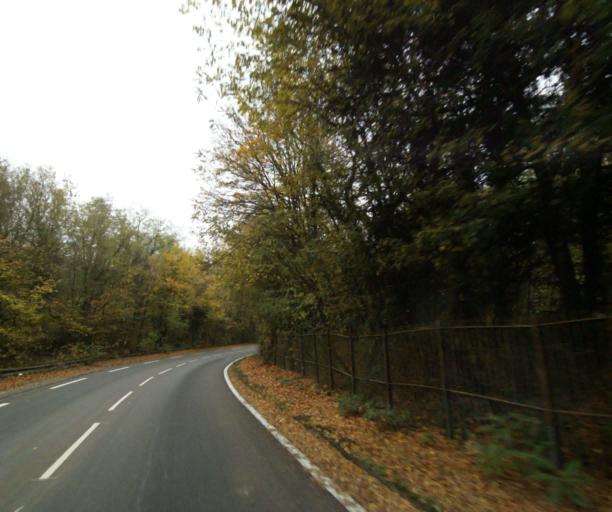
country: FR
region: Lorraine
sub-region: Departement de Meurthe-et-Moselle
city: Joeuf
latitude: 49.2329
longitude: 6.0264
